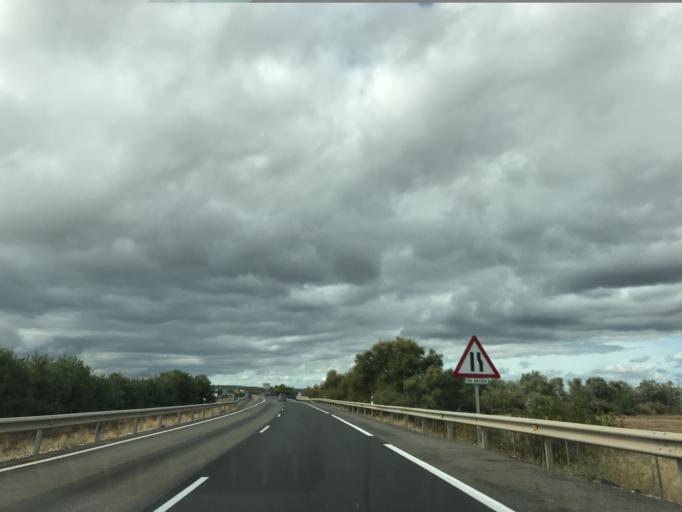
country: ES
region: Andalusia
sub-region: Province of Cordoba
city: Villa del Rio
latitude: 37.9873
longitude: -4.2909
